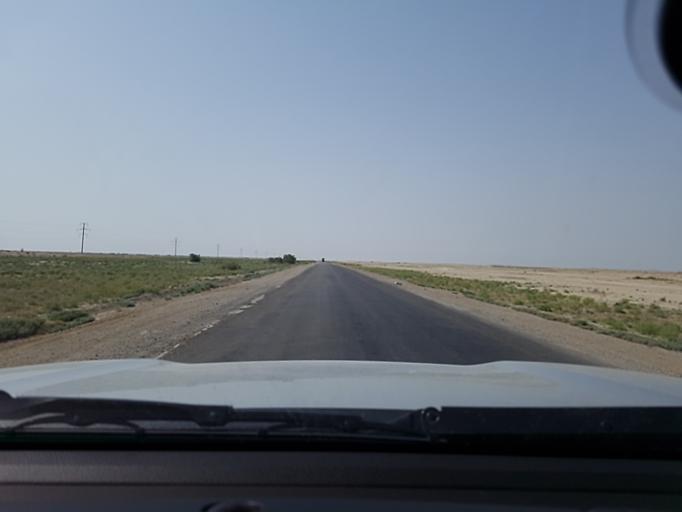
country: TM
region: Balkan
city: Gumdag
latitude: 38.8578
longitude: 54.5949
